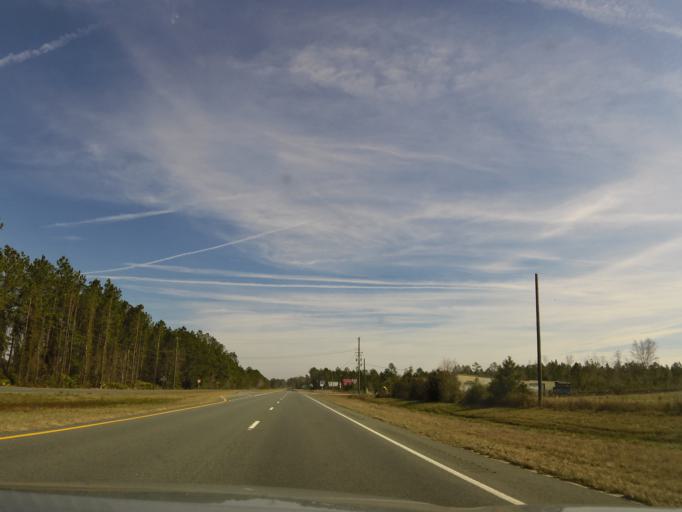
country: US
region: Georgia
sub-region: Brantley County
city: Nahunta
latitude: 31.2003
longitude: -82.0064
